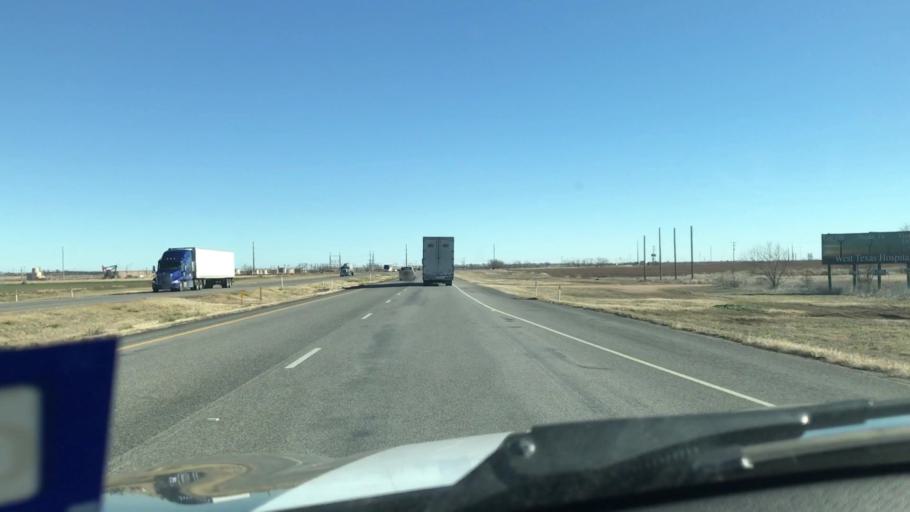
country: US
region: Texas
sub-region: Scurry County
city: Snyder
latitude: 32.7879
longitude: -100.9521
